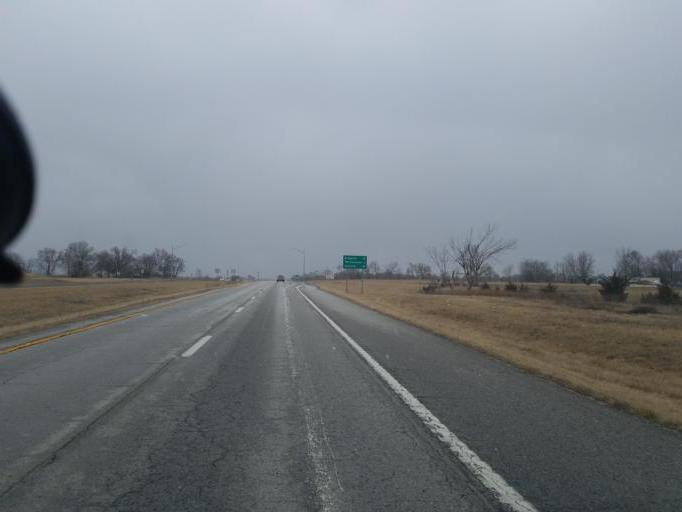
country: US
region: Missouri
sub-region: Macon County
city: La Plata
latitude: 39.9005
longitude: -92.4723
